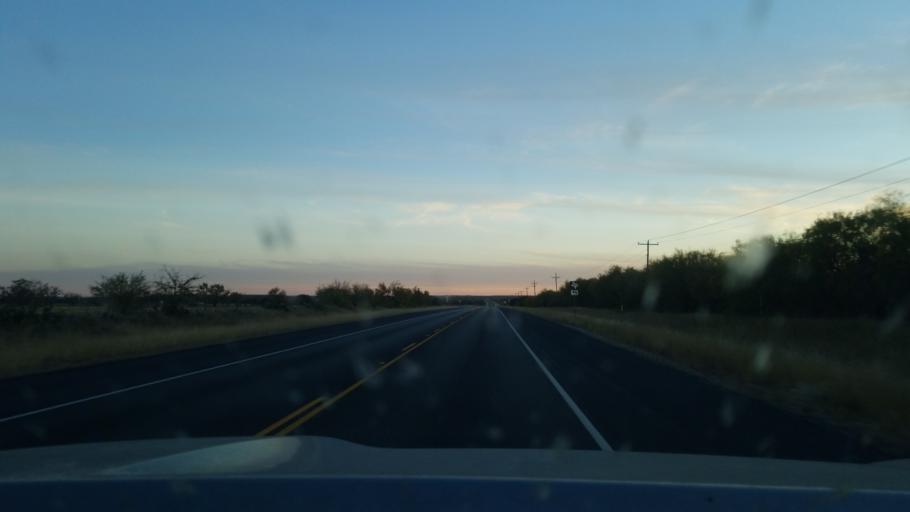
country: US
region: Texas
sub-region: Stephens County
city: Breckenridge
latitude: 32.6660
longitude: -98.9024
